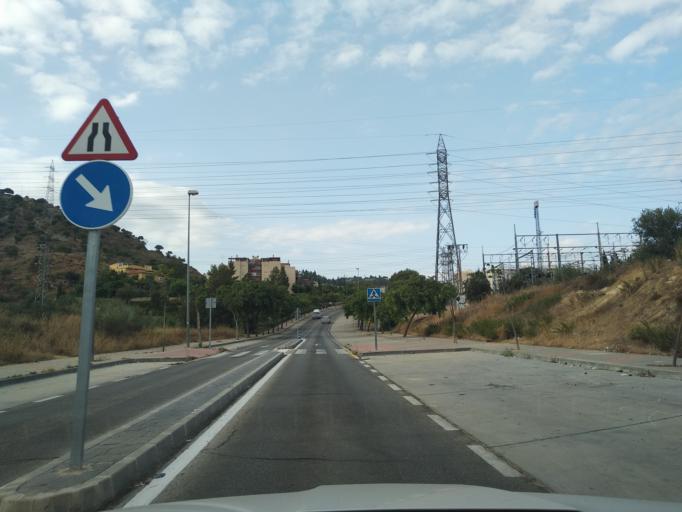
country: ES
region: Andalusia
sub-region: Provincia de Malaga
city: Malaga
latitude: 36.7272
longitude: -4.4745
